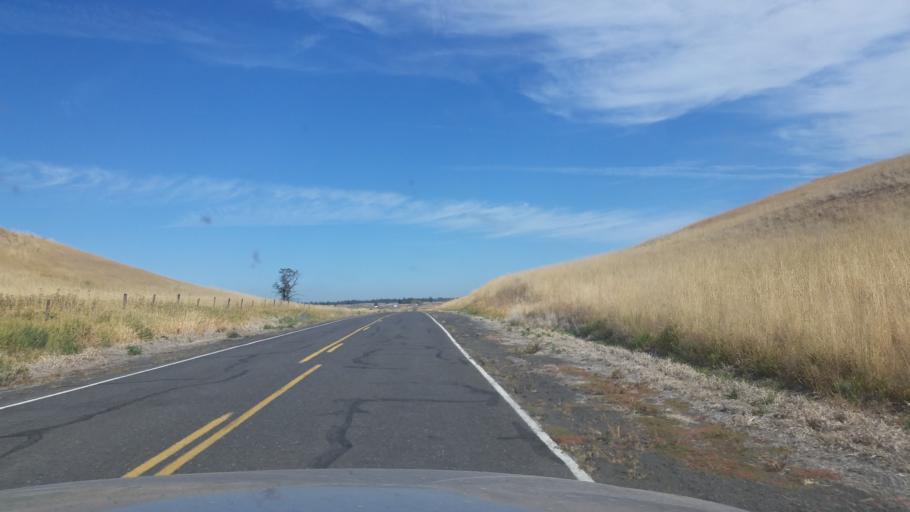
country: US
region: Washington
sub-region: Spokane County
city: Medical Lake
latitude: 47.3805
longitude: -117.8449
